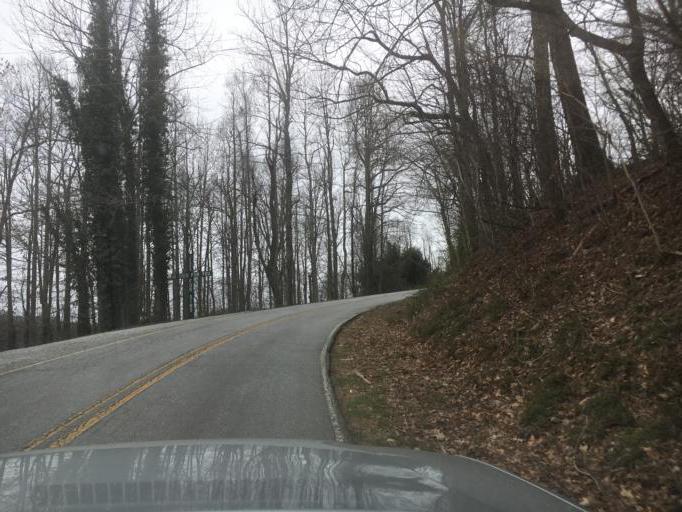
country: US
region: North Carolina
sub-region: Henderson County
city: East Flat Rock
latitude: 35.2459
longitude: -82.4138
